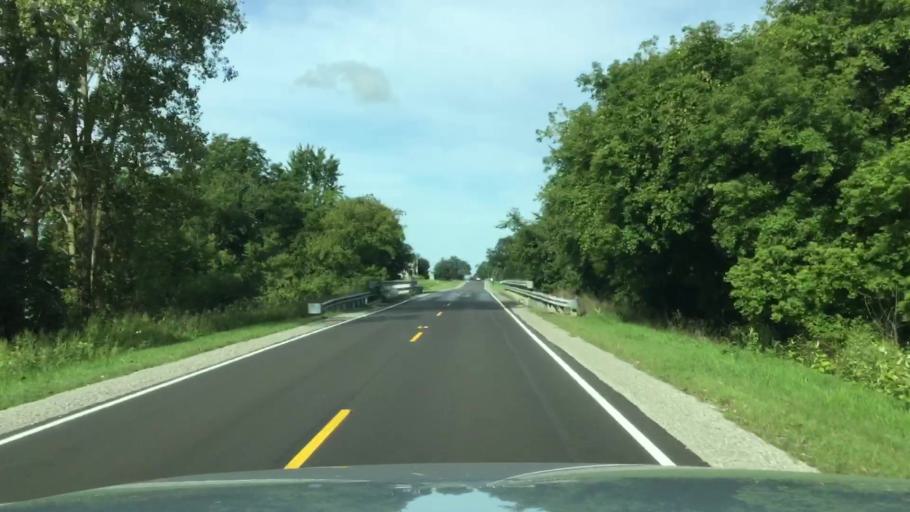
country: US
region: Michigan
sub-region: Genesee County
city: Montrose
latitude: 43.1471
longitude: -83.9387
